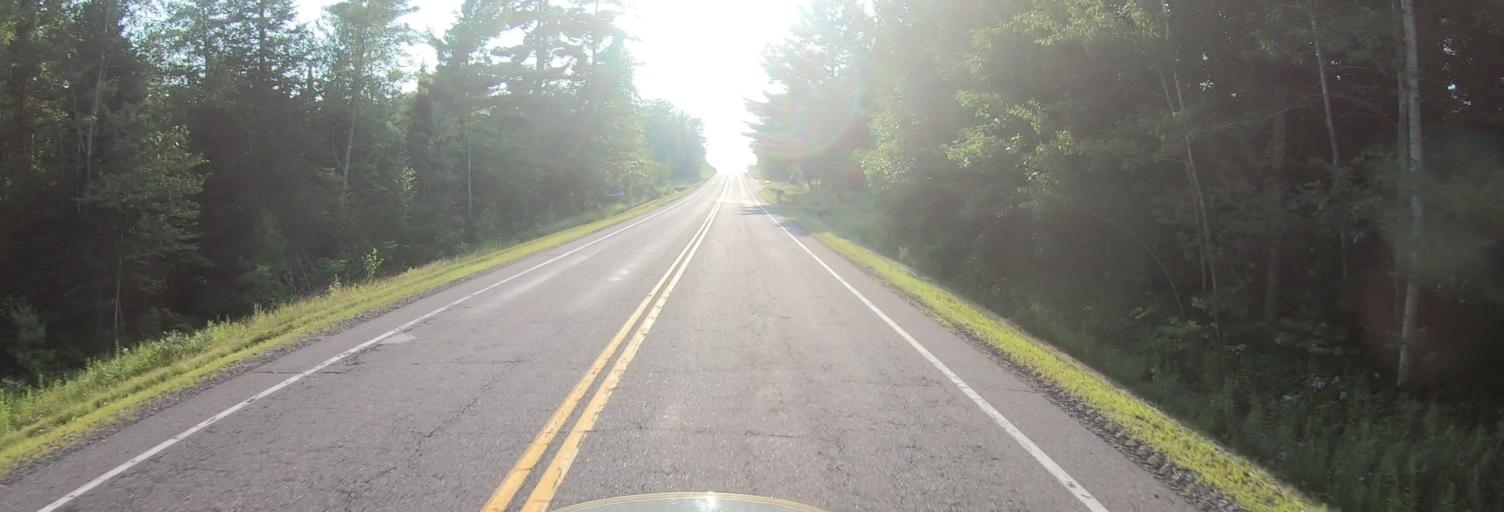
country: US
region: Wisconsin
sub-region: Sawyer County
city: Little Round Lake
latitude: 46.0737
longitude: -91.0499
